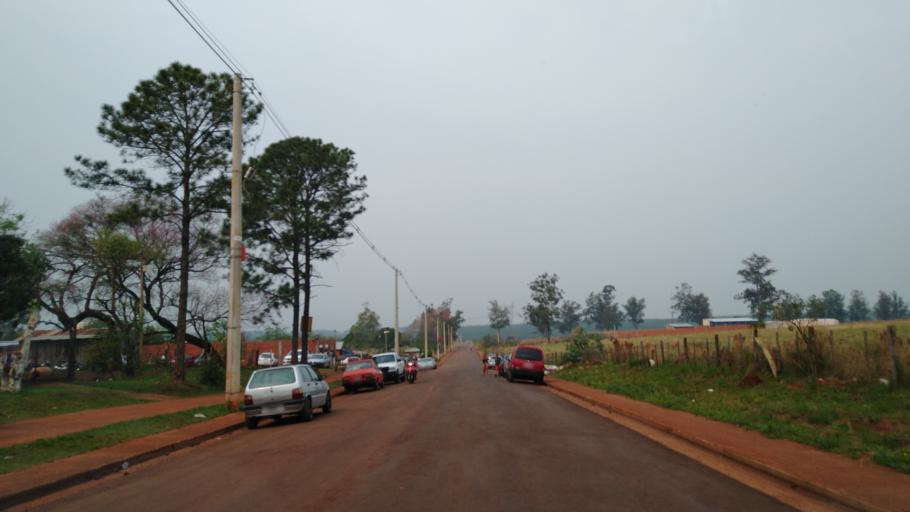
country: AR
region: Misiones
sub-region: Departamento de Capital
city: Posadas
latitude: -27.4453
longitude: -55.9333
